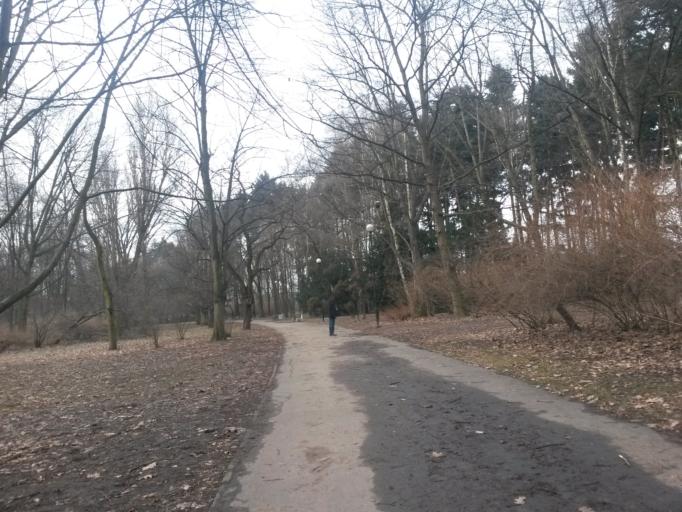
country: PL
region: Masovian Voivodeship
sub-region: Warszawa
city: Ochota
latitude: 52.2041
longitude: 20.9921
